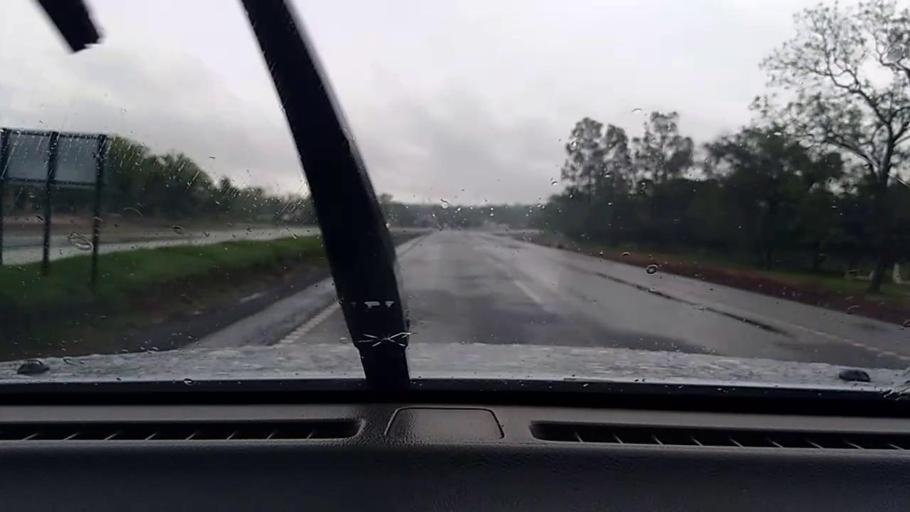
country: PY
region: Caaguazu
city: Repatriacion
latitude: -25.4647
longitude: -55.9315
